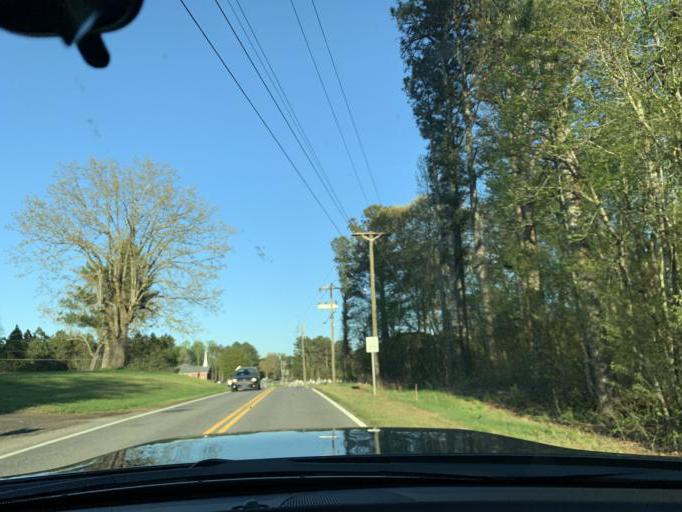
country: US
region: Georgia
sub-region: Forsyth County
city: Cumming
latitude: 34.2440
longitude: -84.1893
